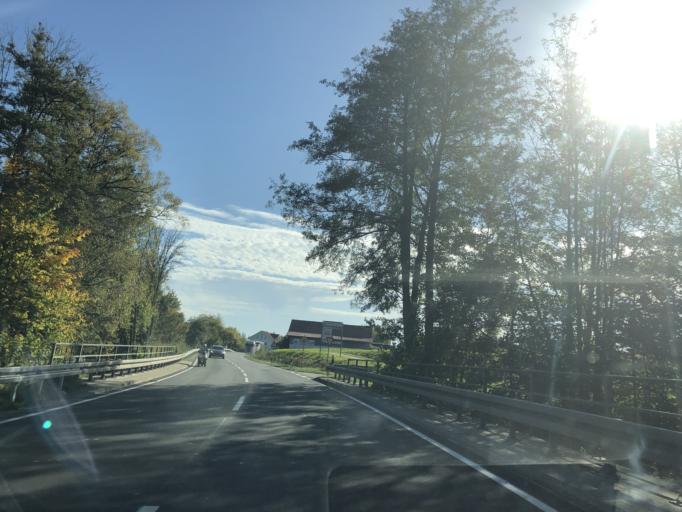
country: DE
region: Bavaria
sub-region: Lower Bavaria
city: Grafling
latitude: 48.8771
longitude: 12.9614
